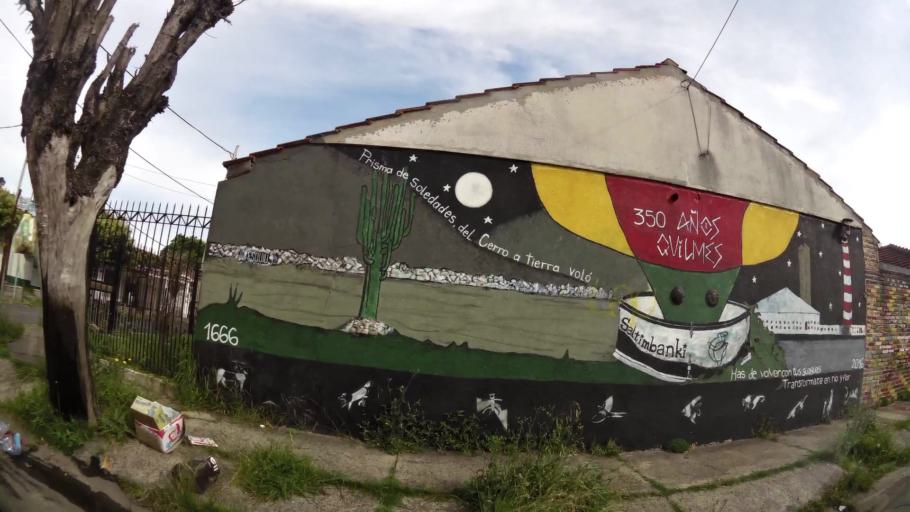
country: AR
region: Buenos Aires
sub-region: Partido de Quilmes
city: Quilmes
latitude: -34.7516
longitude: -58.2750
